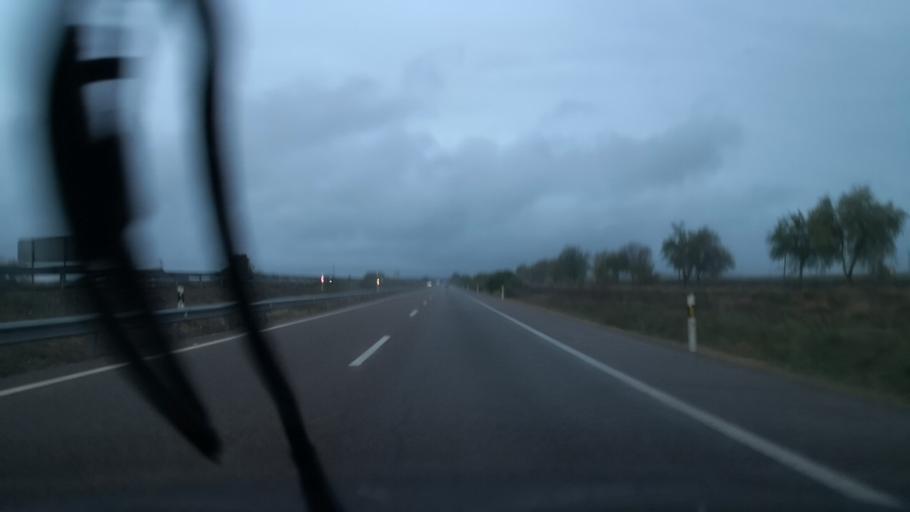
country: ES
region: Extremadura
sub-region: Provincia de Badajoz
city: Arroyo de San Servan
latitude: 38.8820
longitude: -6.4419
